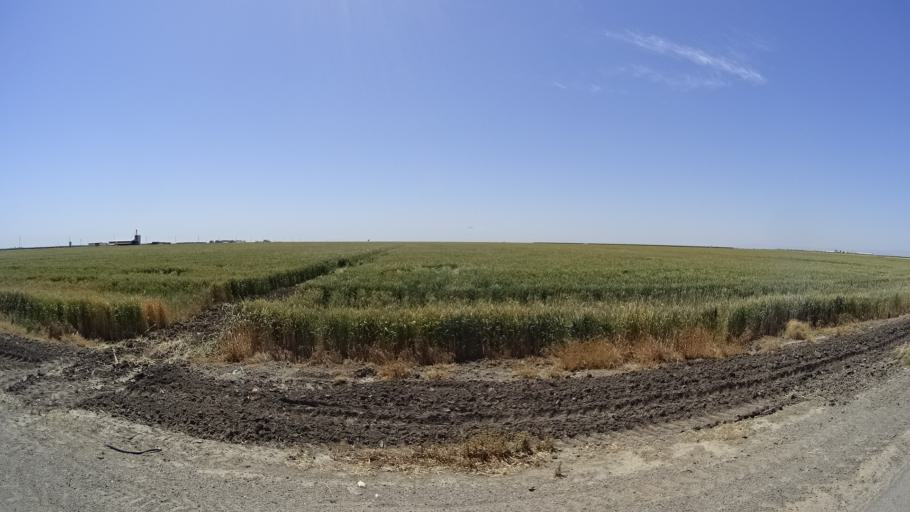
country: US
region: California
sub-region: Kings County
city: Corcoran
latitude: 36.1379
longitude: -119.6501
